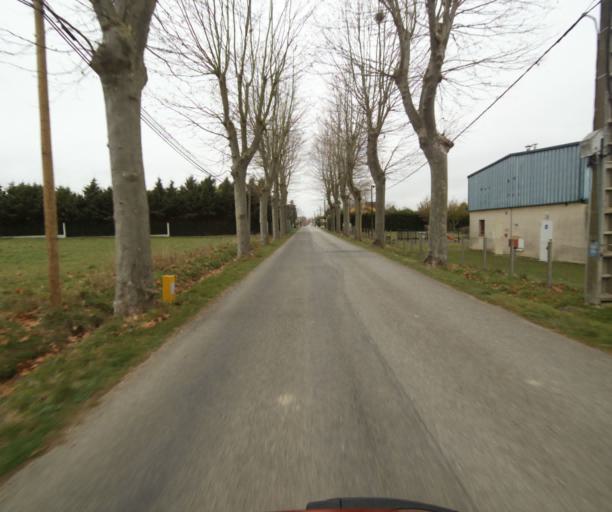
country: FR
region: Midi-Pyrenees
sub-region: Departement de la Haute-Garonne
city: Gaillac-Toulza
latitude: 43.2738
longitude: 1.5057
